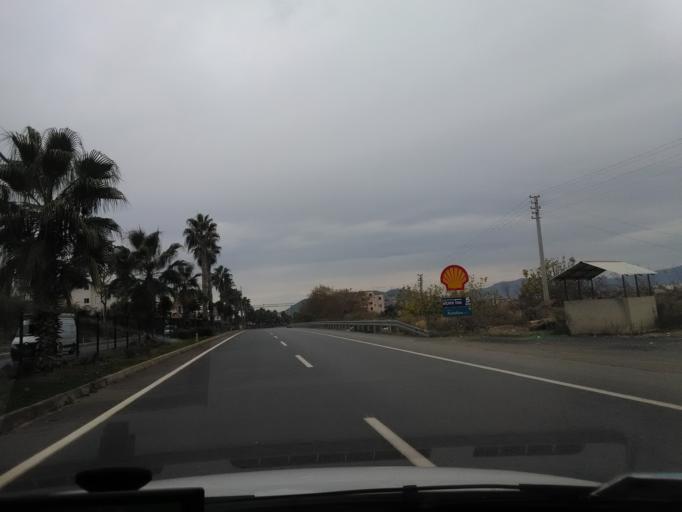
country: TR
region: Antalya
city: Gazipasa
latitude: 36.2557
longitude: 32.3309
